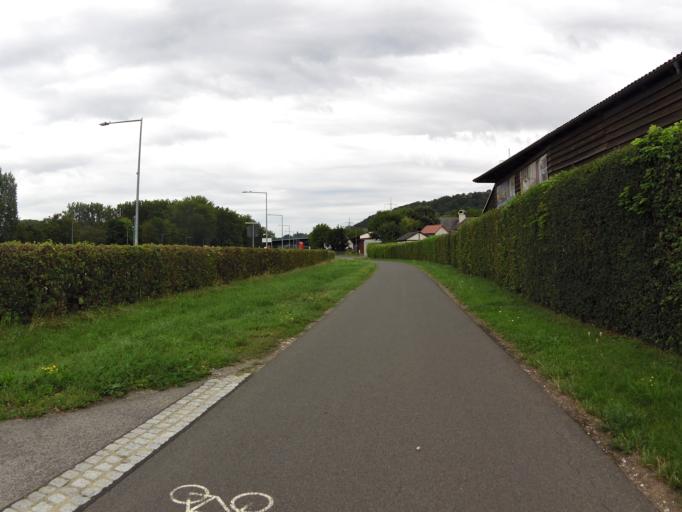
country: DE
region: Bavaria
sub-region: Regierungsbezirk Unterfranken
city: Eltmann
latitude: 49.9799
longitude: 10.6409
